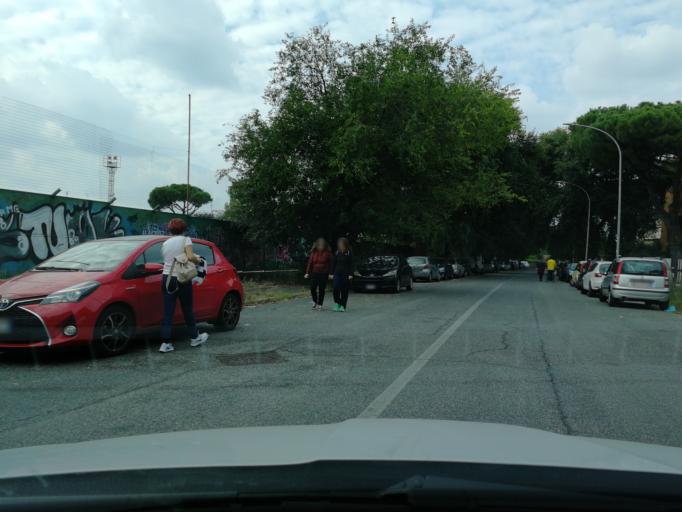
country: IT
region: Latium
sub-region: Citta metropolitana di Roma Capitale
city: Rome
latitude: 41.8581
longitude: 12.5491
